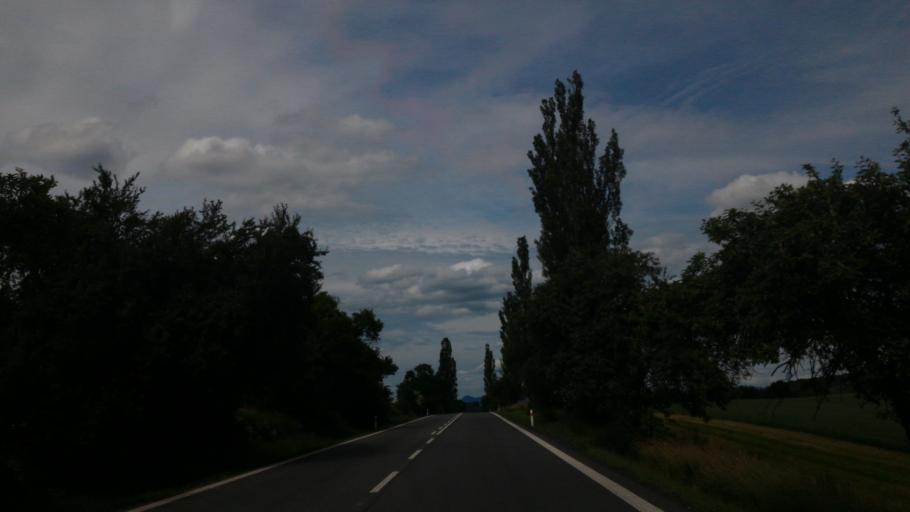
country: CZ
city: Duba
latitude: 50.5711
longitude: 14.5445
